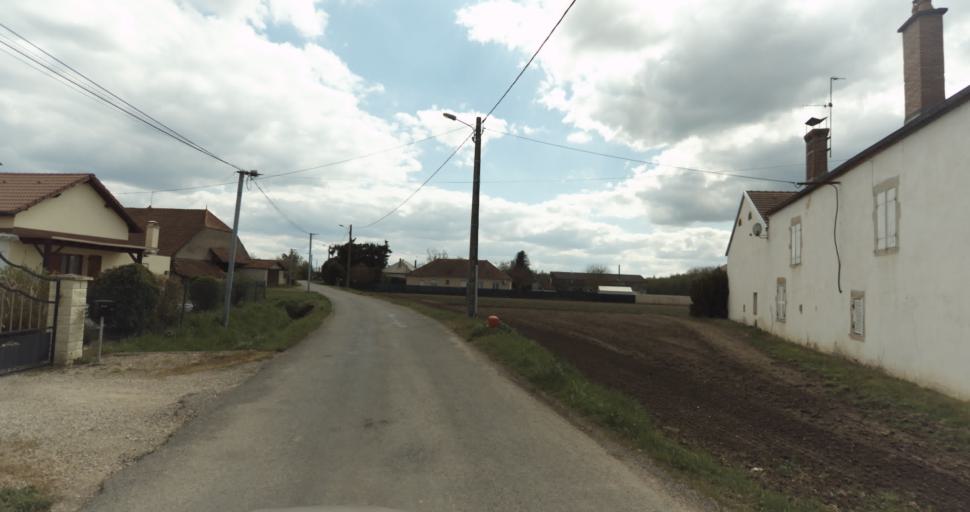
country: FR
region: Bourgogne
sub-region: Departement de la Cote-d'Or
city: Auxonne
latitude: 47.1823
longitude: 5.3914
